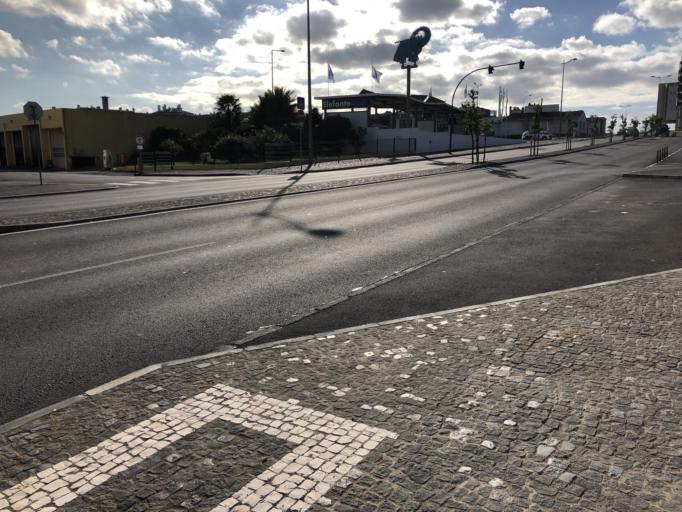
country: PT
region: Azores
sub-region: Ponta Delgada
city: Rosto de Cao
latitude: 37.7516
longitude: -25.6560
